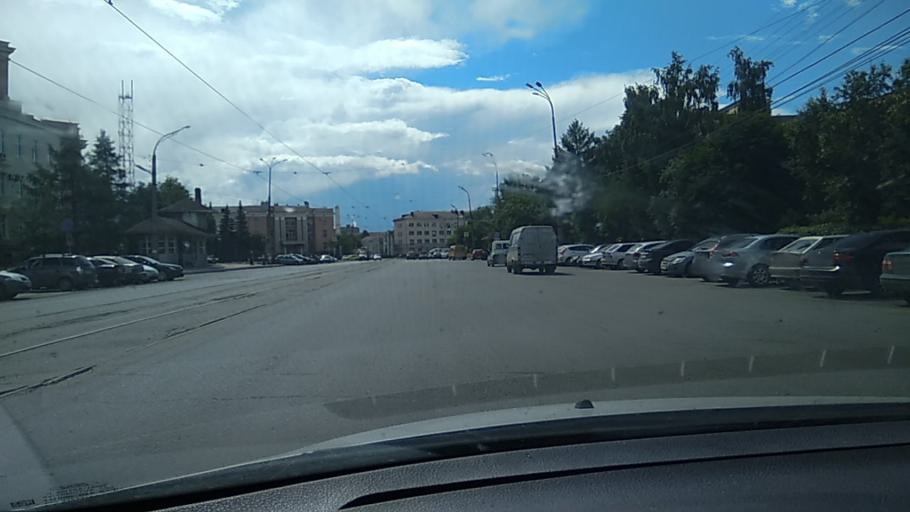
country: RU
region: Sverdlovsk
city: Nizhniy Tagil
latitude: 57.9297
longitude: 60.0130
